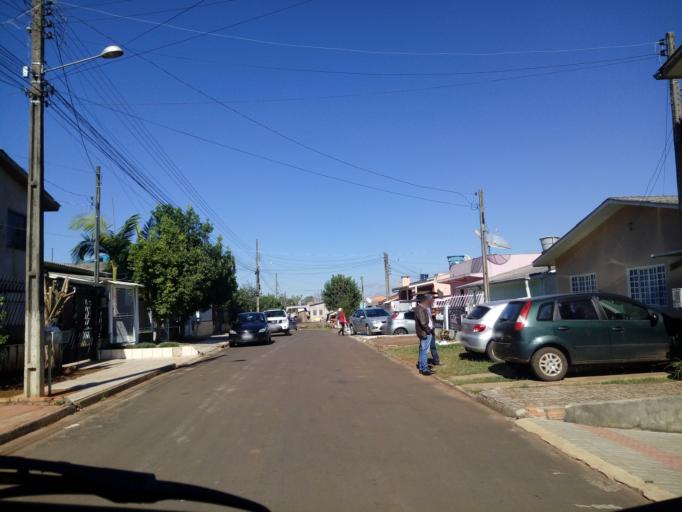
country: BR
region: Santa Catarina
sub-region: Chapeco
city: Chapeco
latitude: -27.0928
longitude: -52.6821
